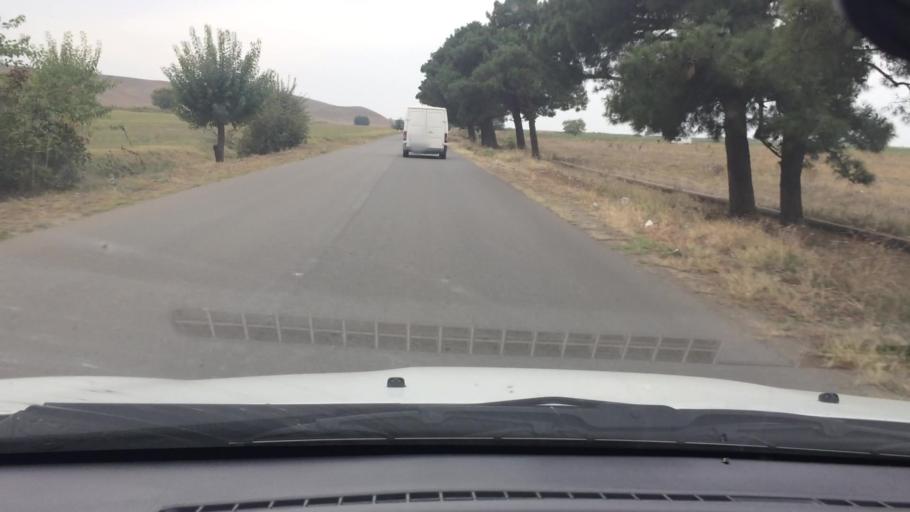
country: AM
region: Tavush
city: Berdavan
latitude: 41.3352
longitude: 45.0276
